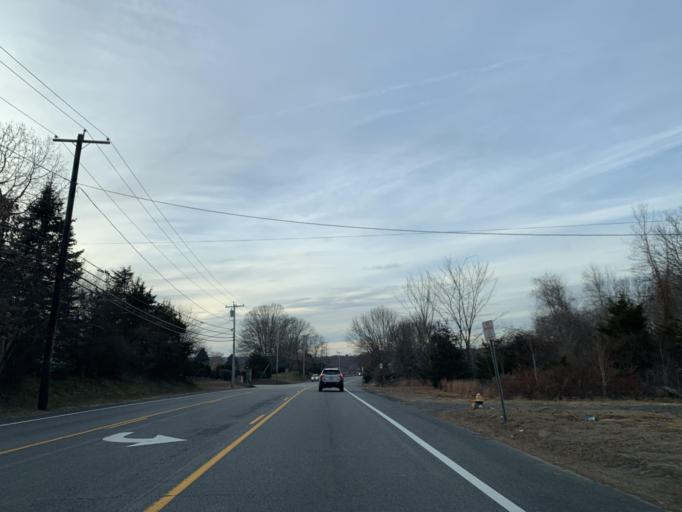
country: US
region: Rhode Island
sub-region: Providence County
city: Greenville
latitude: 41.8787
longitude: -71.5738
